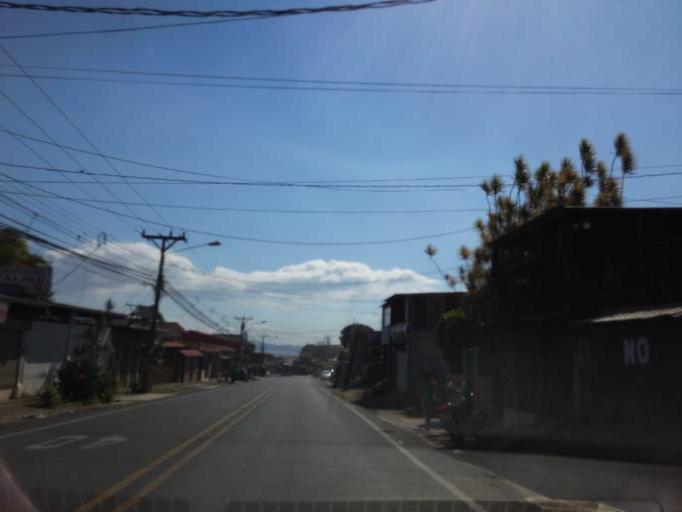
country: CR
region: Alajuela
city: Alajuela
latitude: 10.0270
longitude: -84.2059
